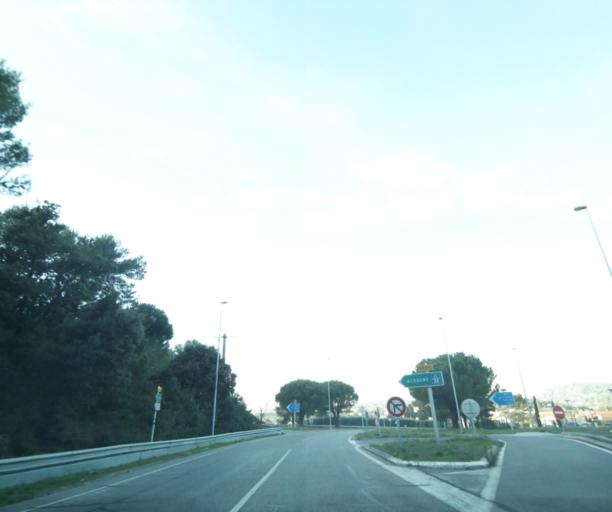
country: FR
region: Provence-Alpes-Cote d'Azur
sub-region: Departement des Bouches-du-Rhone
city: Roquefort-la-Bedoule
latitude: 43.2424
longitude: 5.5935
